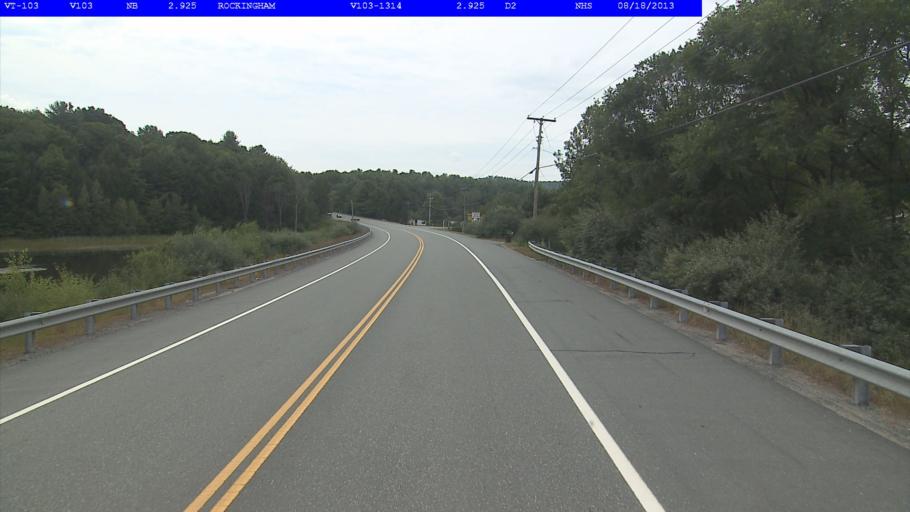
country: US
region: Vermont
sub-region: Windham County
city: Rockingham
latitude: 43.2000
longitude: -72.5072
